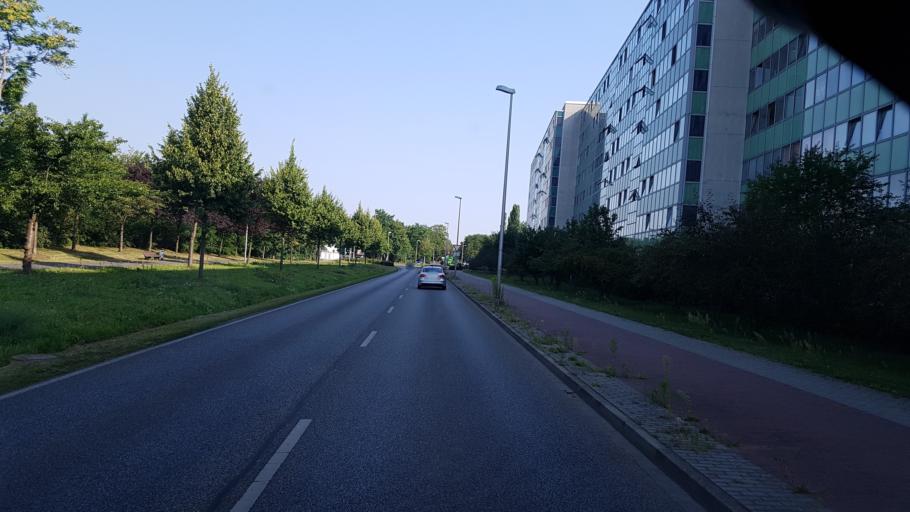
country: DE
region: Brandenburg
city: Cottbus
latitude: 51.7635
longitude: 14.3131
